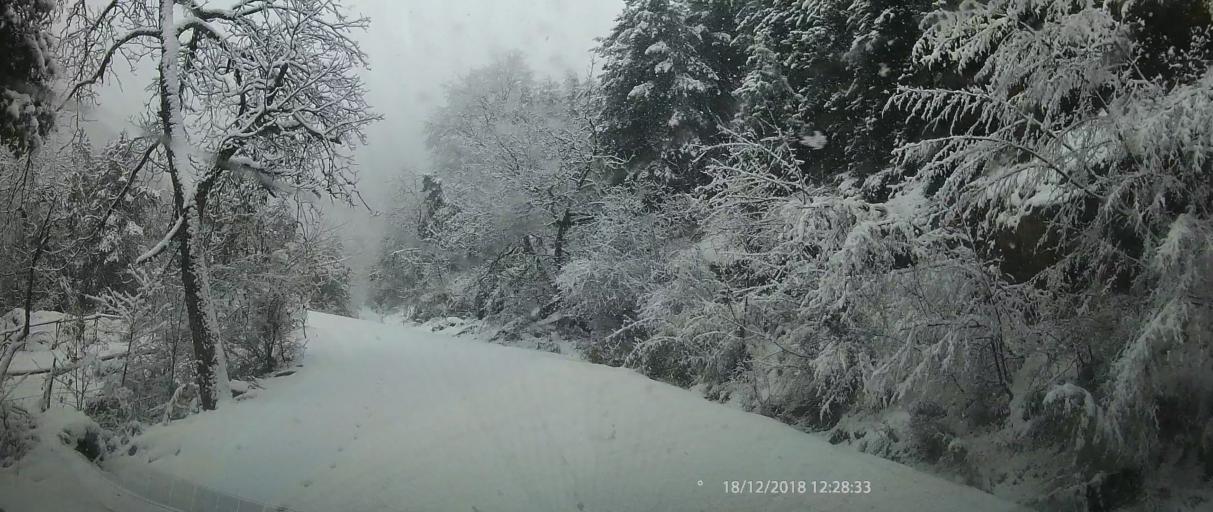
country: GR
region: Central Macedonia
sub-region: Nomos Pierias
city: Litochoro
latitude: 40.0863
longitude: 22.4069
